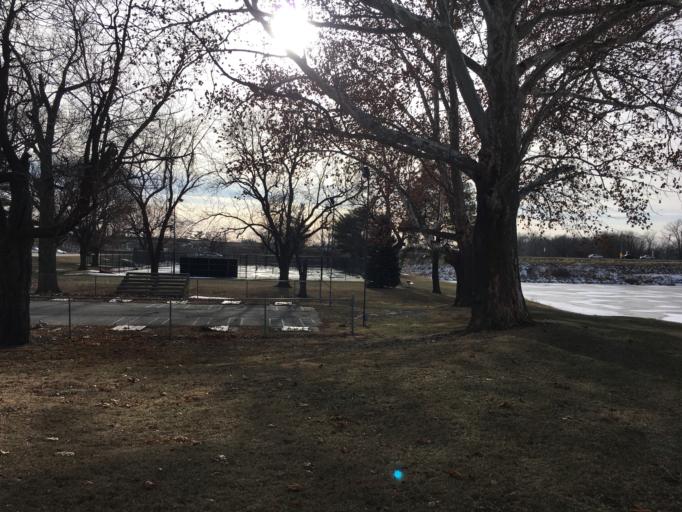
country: US
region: Iowa
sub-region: Wapello County
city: Ottumwa
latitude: 41.0135
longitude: -92.4160
